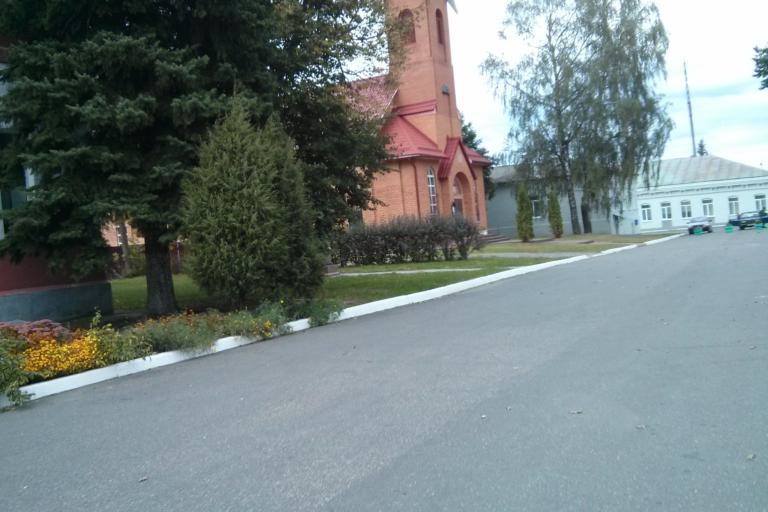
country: BY
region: Minsk
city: Chervyen'
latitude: 53.7146
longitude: 28.4156
